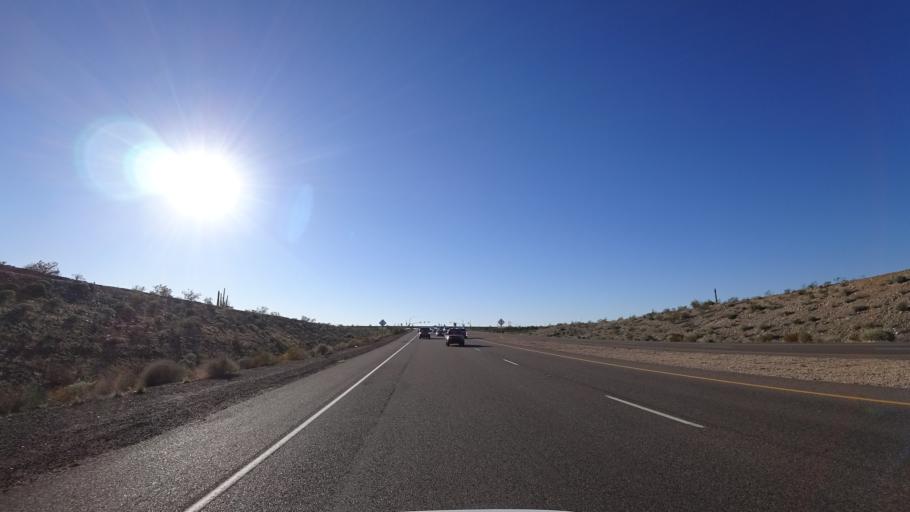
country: US
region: Arizona
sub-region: Maricopa County
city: Sun City West
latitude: 33.7136
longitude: -112.3029
